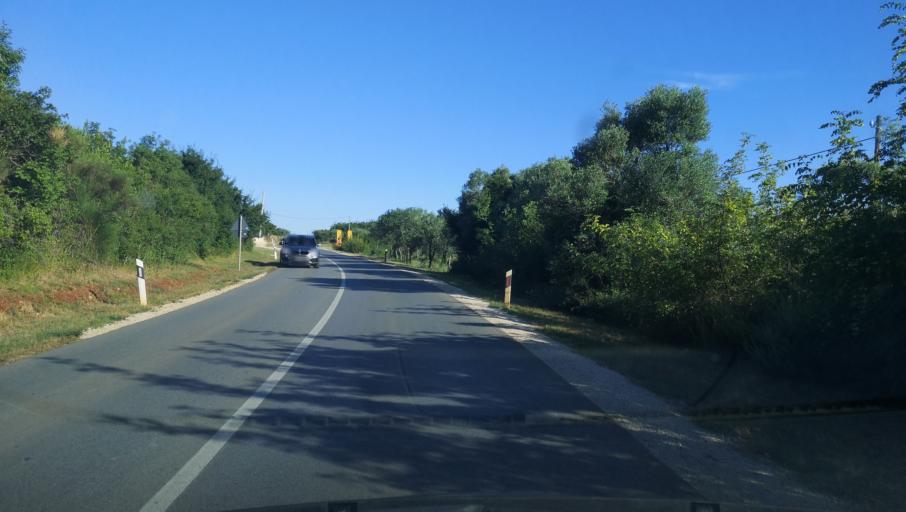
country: HR
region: Istarska
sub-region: Grad Rovinj
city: Rovinj
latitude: 45.0773
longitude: 13.6761
